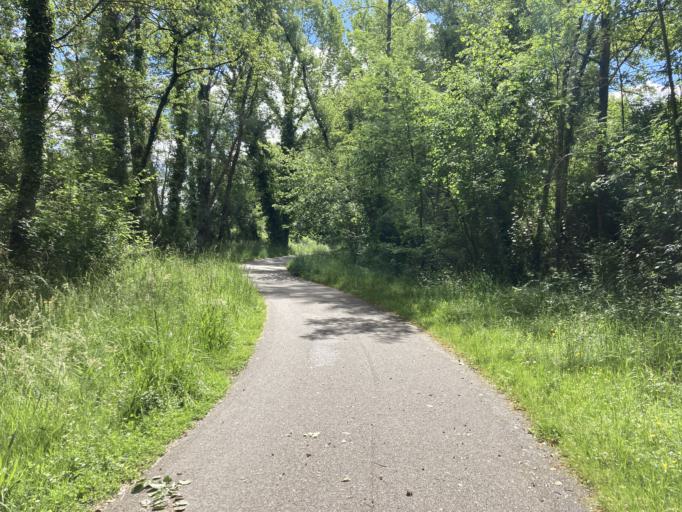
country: FR
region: Aquitaine
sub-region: Departement des Pyrenees-Atlantiques
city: Billere
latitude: 43.3003
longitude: -0.4239
